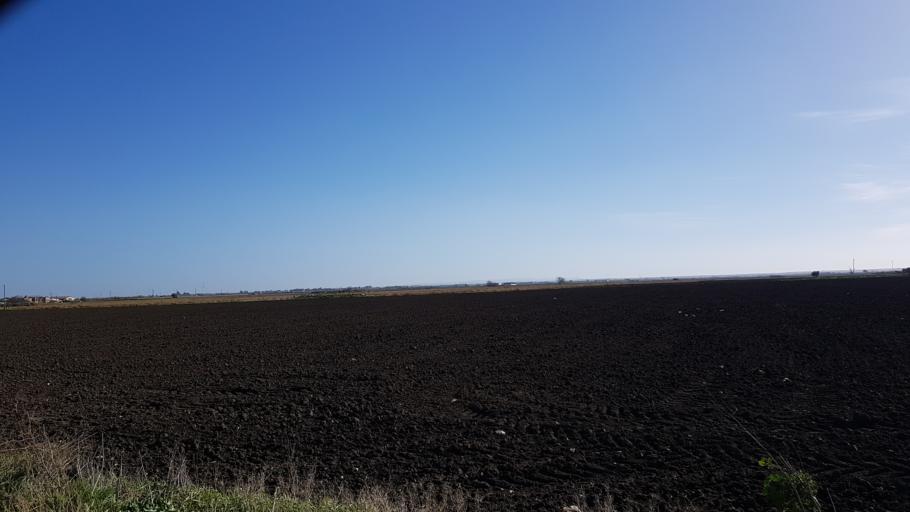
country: IT
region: Apulia
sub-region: Provincia di Foggia
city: Carapelle
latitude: 41.3819
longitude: 15.6448
